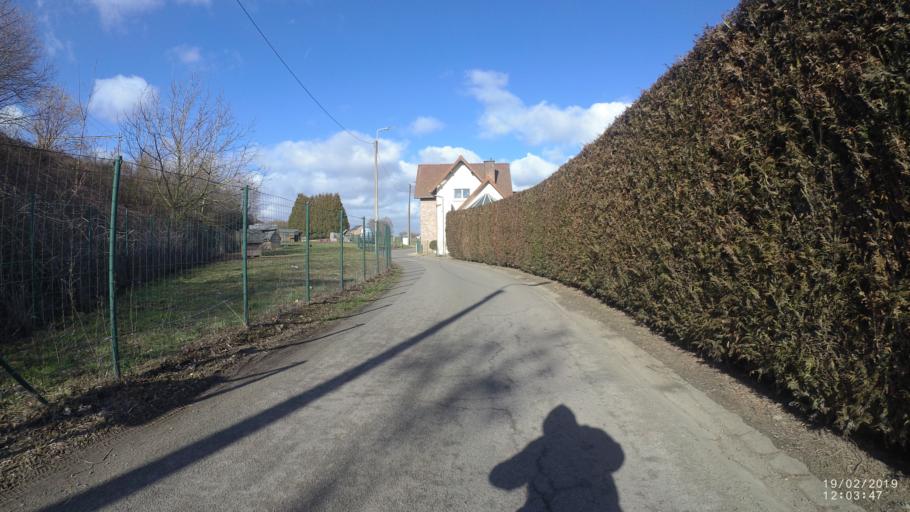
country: BE
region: Wallonia
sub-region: Province de Liege
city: Juprelle
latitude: 50.7525
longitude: 5.5347
